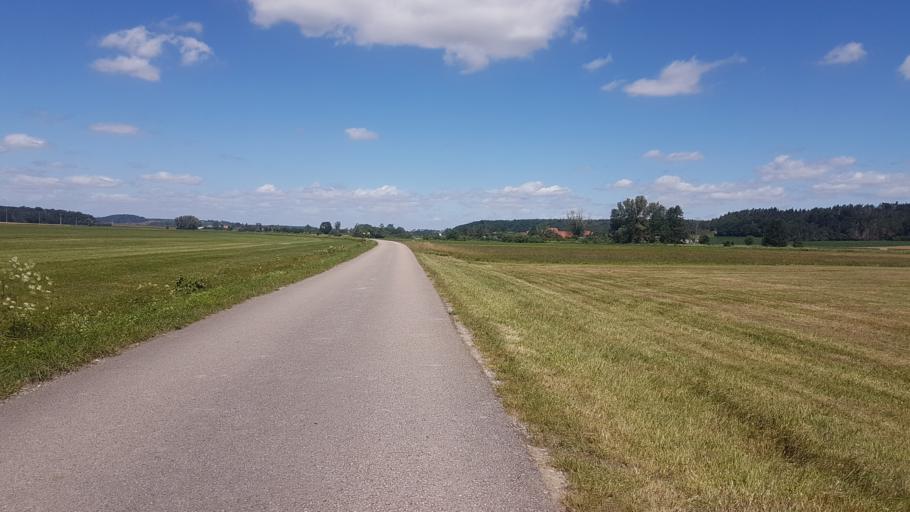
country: DE
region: Bavaria
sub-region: Regierungsbezirk Mittelfranken
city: Aurach
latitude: 49.2690
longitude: 10.4428
